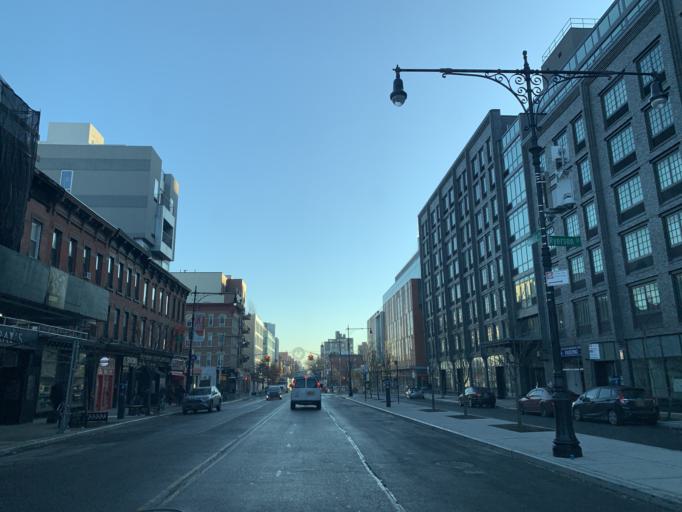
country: US
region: New York
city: New York City
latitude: 40.6936
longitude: -73.9650
